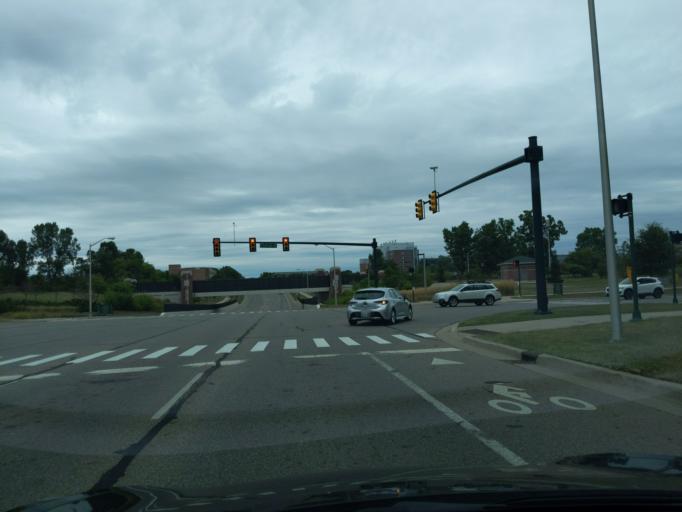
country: US
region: Michigan
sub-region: Ingham County
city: East Lansing
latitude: 42.7187
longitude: -84.4782
